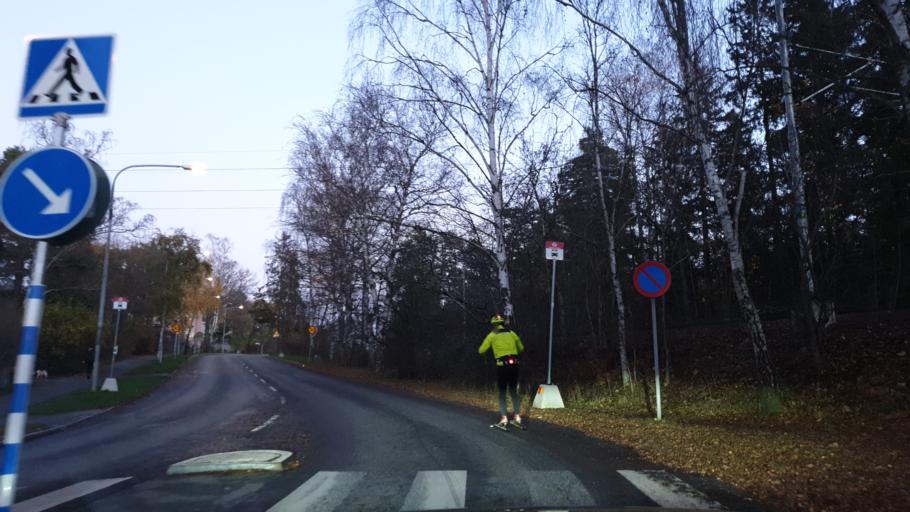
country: SE
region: Stockholm
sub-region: Stockholms Kommun
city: Bromma
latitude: 59.3295
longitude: 17.9236
